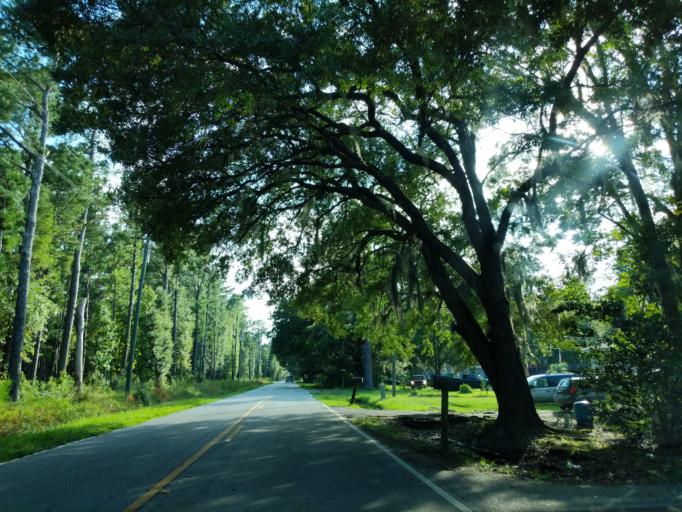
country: US
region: South Carolina
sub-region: Charleston County
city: Awendaw
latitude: 33.1403
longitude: -79.4239
